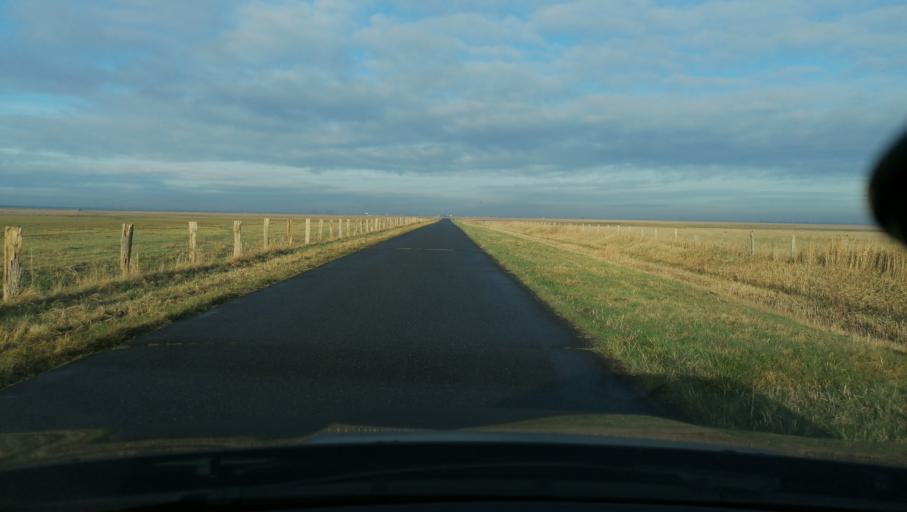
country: DE
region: Schleswig-Holstein
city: Friedrichsgabekoog
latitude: 54.1069
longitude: 8.9533
